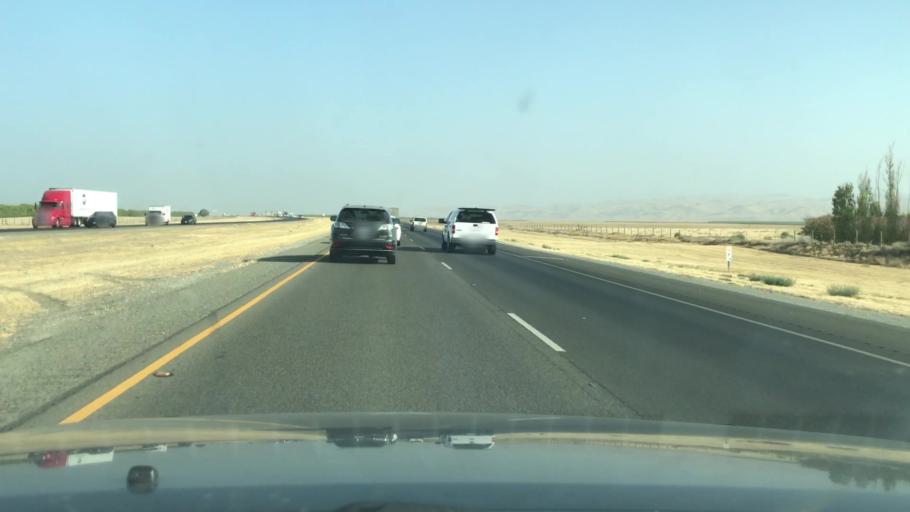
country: US
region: California
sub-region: Fresno County
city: Mendota
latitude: 36.6272
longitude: -120.6143
